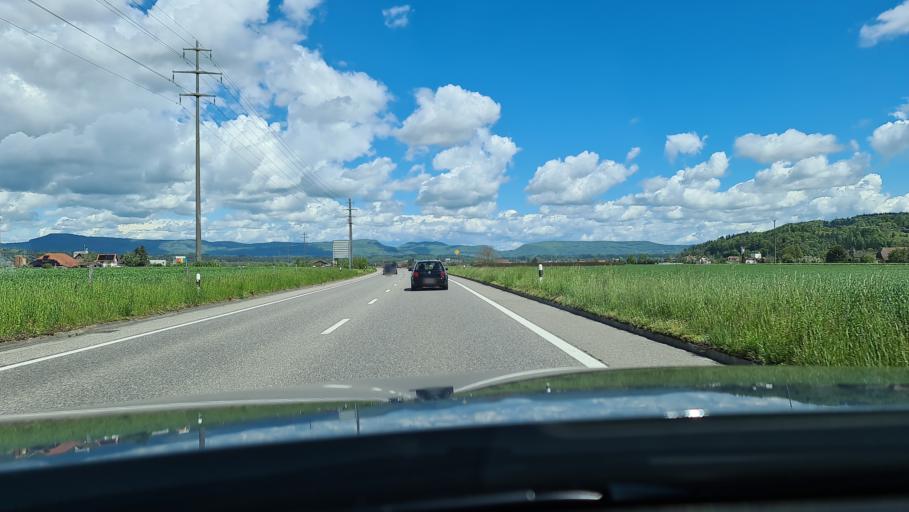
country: CH
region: Aargau
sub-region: Bezirk Kulm
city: Schoftland
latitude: 47.3216
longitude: 8.0473
